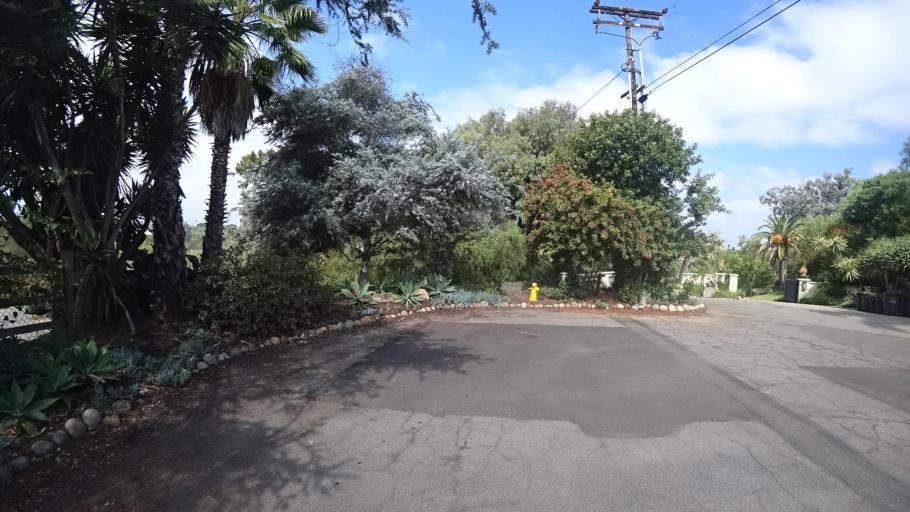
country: US
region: California
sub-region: San Diego County
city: Rancho Santa Fe
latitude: 33.0321
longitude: -117.2087
